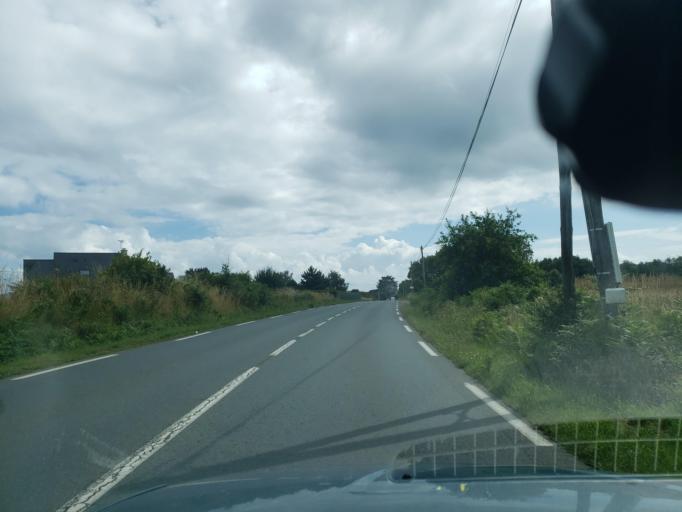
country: FR
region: Brittany
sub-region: Departement du Finistere
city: Plomeur
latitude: 47.8360
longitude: -4.2855
